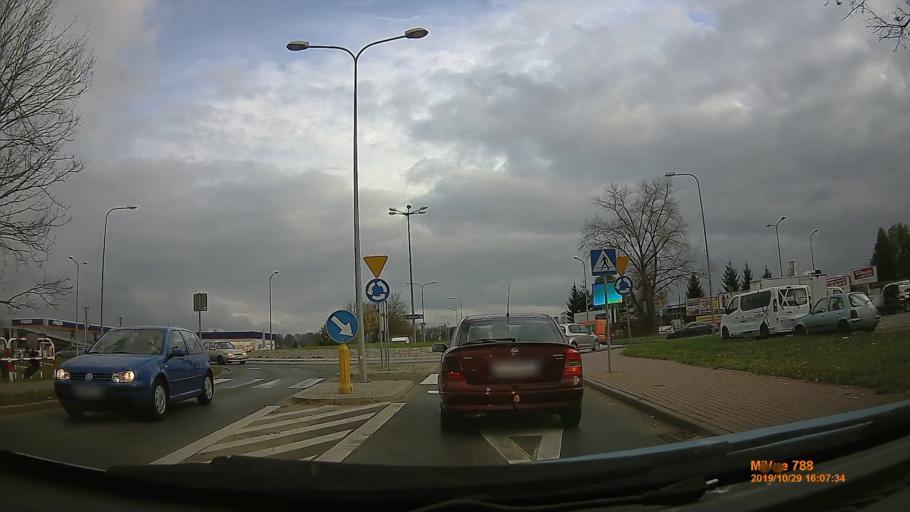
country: PL
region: Lower Silesian Voivodeship
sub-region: Powiat klodzki
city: Klodzko
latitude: 50.4503
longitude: 16.6391
